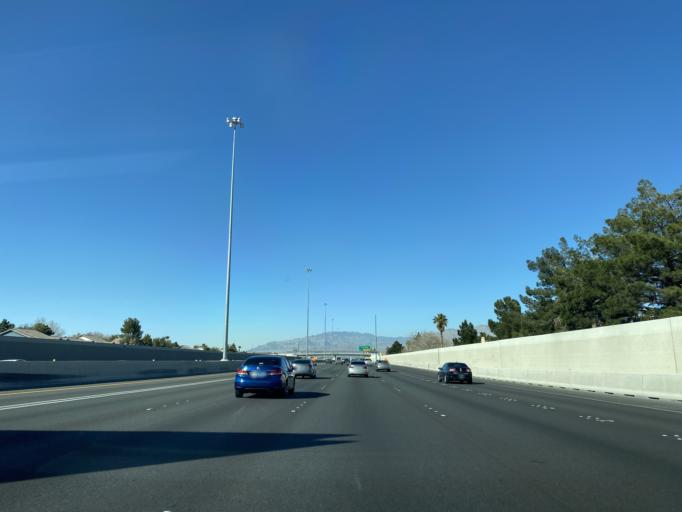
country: US
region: Nevada
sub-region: Clark County
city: Spring Valley
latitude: 36.2286
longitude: -115.2467
